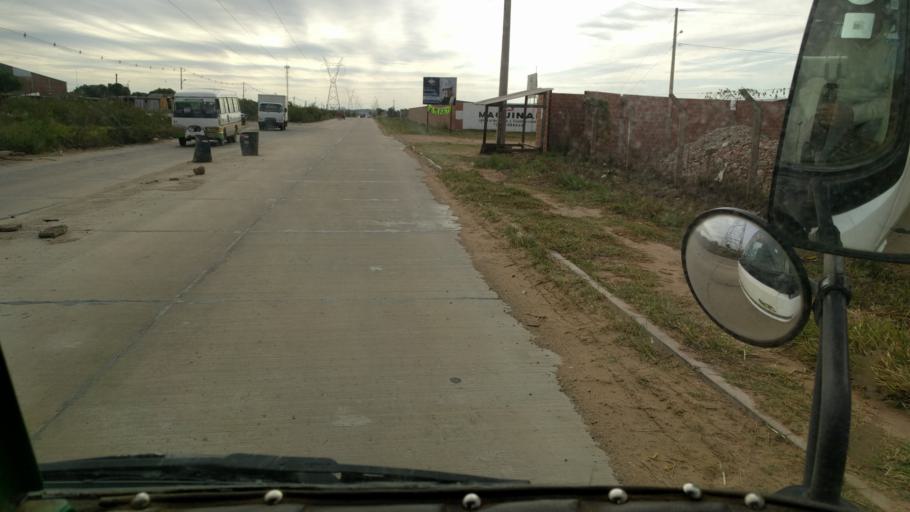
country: BO
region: Santa Cruz
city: Santa Cruz de la Sierra
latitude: -17.6884
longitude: -63.1446
